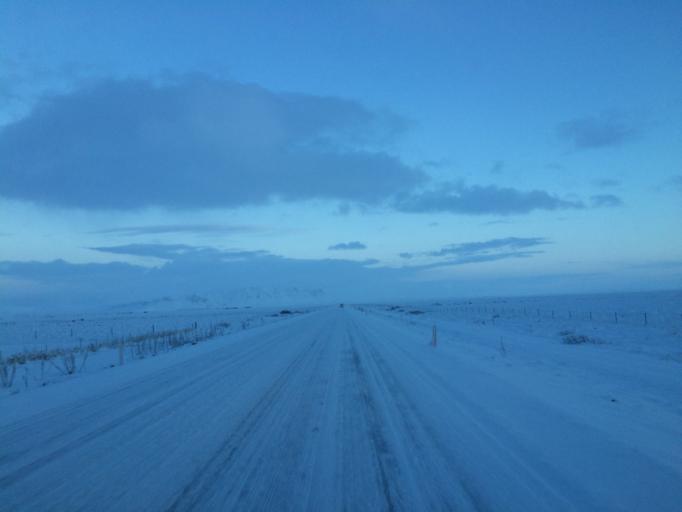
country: IS
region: South
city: Selfoss
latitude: 63.8665
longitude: -21.1030
